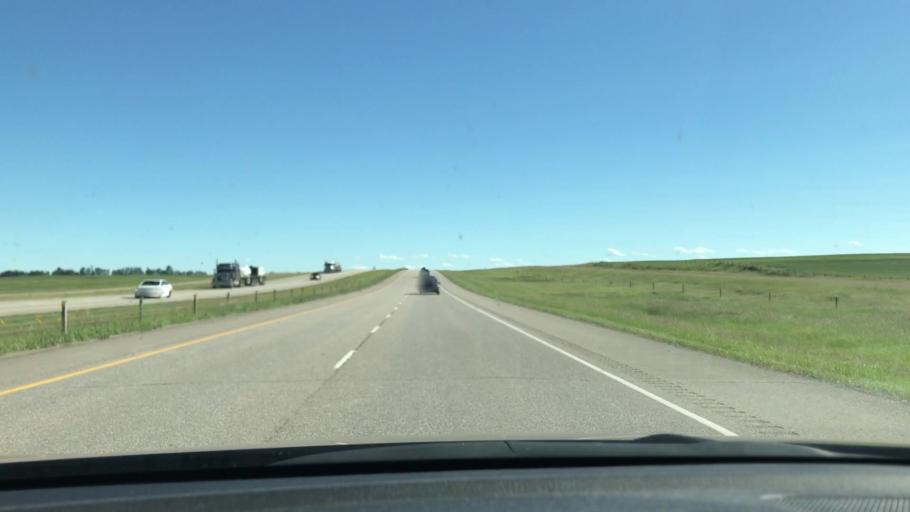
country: CA
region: Alberta
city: Carstairs
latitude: 51.6341
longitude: -114.0256
